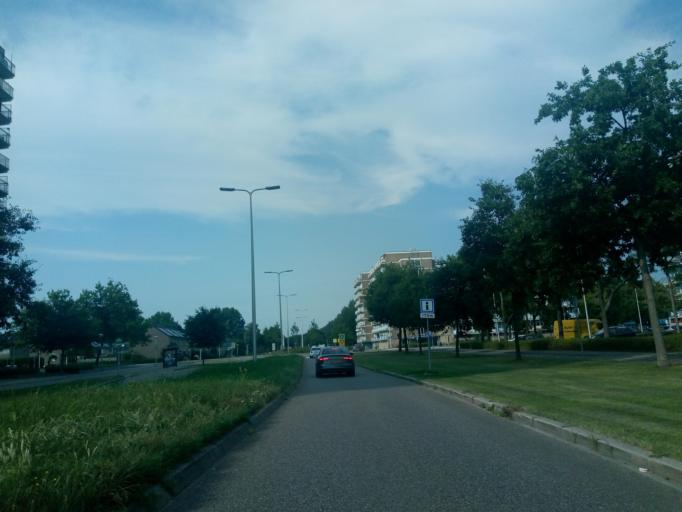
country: NL
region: South Holland
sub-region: Gemeente Alphen aan den Rijn
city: Alphen aan den Rijn
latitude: 52.1443
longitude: 4.6765
